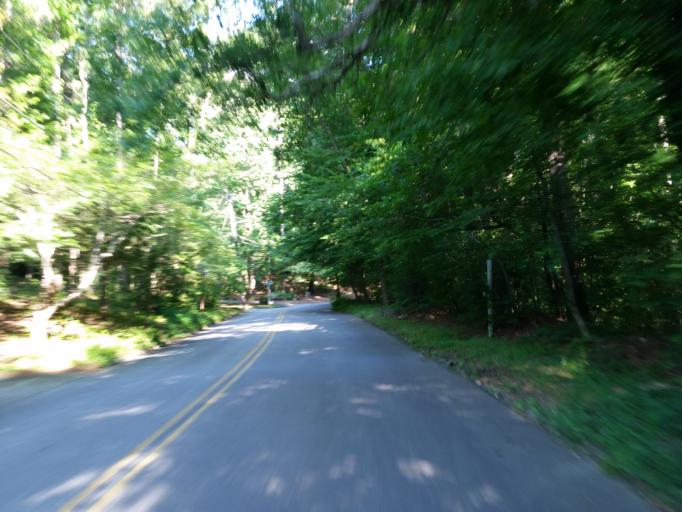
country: US
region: Georgia
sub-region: Cobb County
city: Vinings
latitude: 33.8590
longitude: -84.4236
